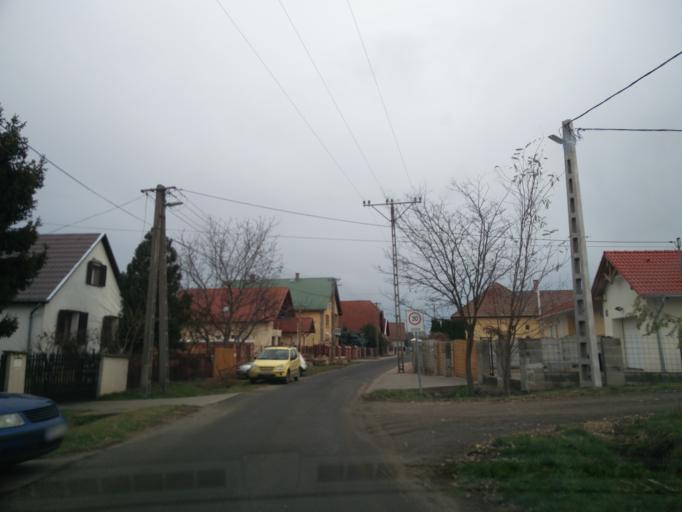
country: HU
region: Pest
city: Fot
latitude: 47.6577
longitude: 19.2296
